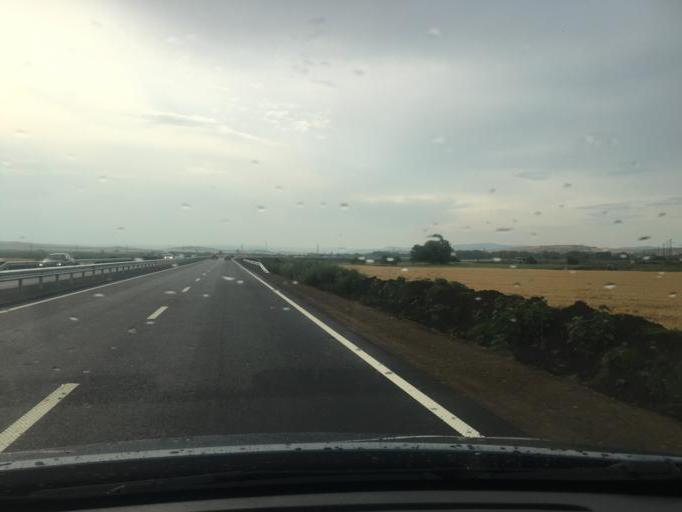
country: BG
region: Burgas
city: Aheloy
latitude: 42.6414
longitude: 27.6387
